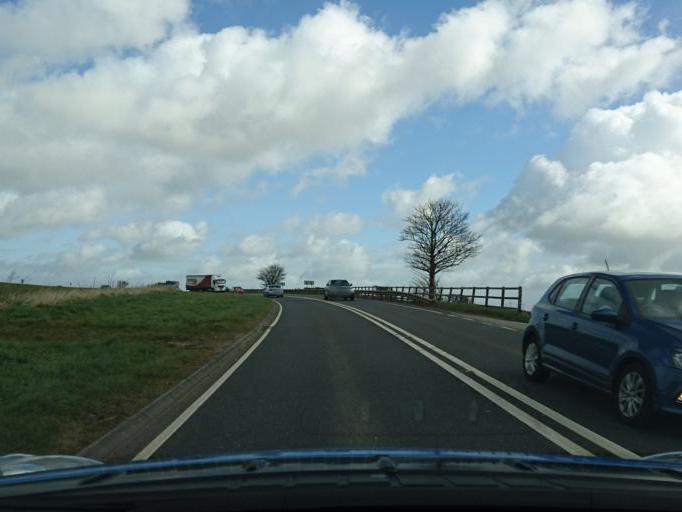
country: GB
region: England
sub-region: South Gloucestershire
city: Cold Ashton
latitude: 51.4642
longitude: -2.3654
